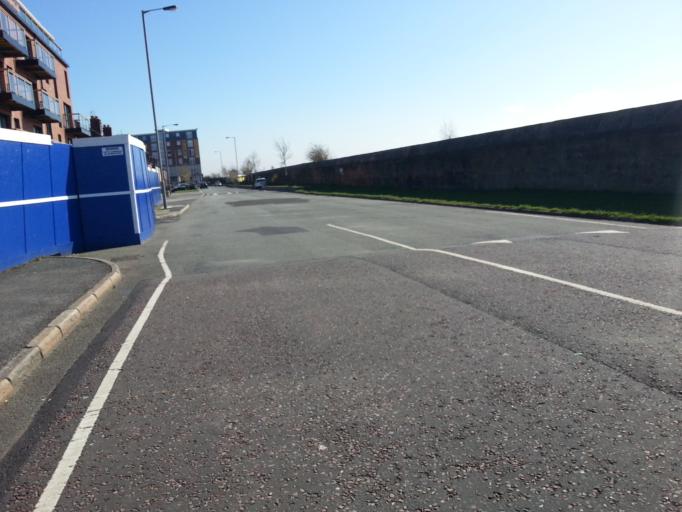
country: GB
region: England
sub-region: Liverpool
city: Liverpool
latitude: 53.3842
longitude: -2.9765
